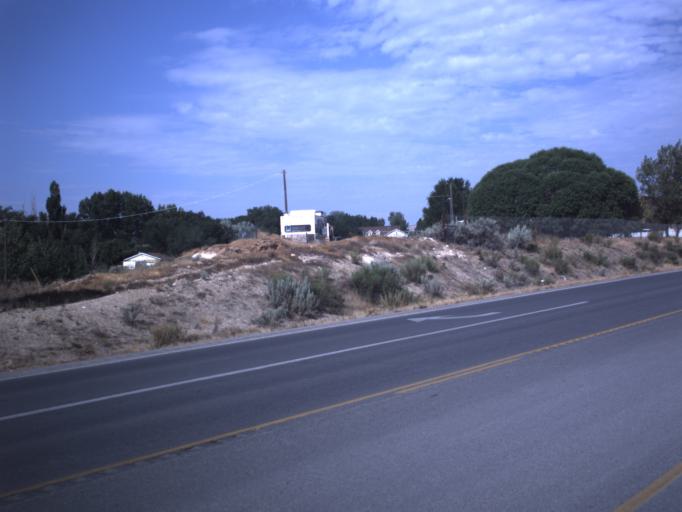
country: US
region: Utah
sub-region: Uintah County
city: Naples
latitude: 40.4062
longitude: -109.4803
